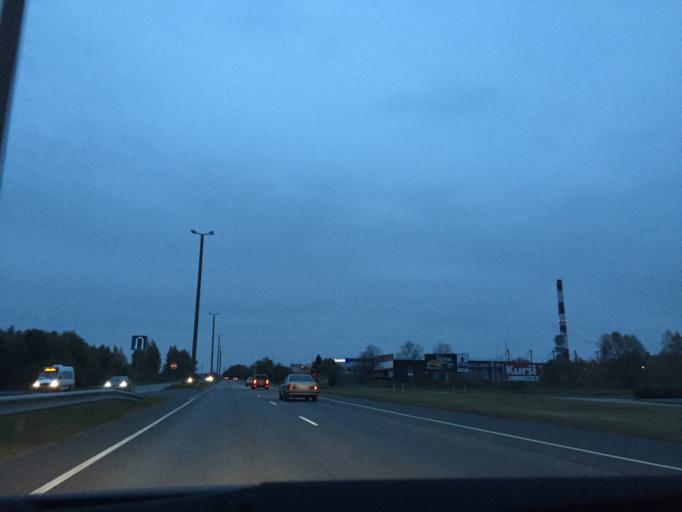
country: LV
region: Marupe
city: Marupe
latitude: 56.8828
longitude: 24.0730
